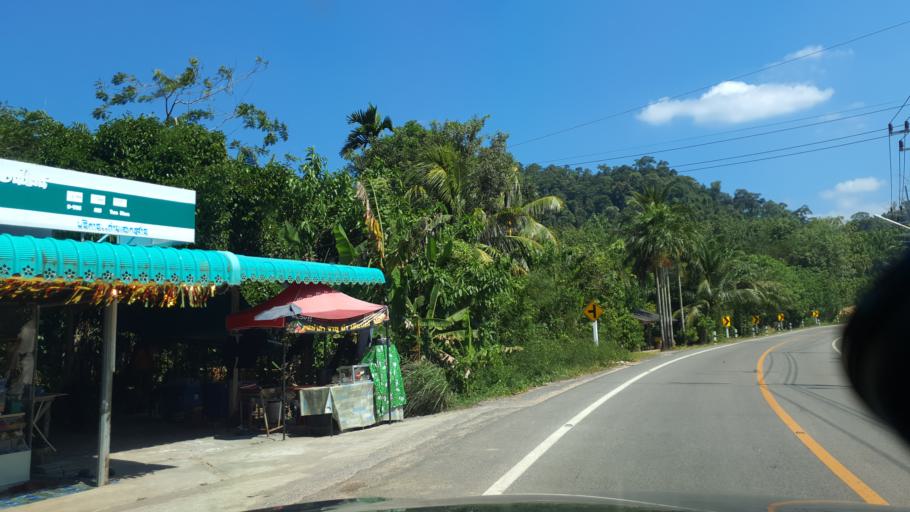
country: TH
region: Krabi
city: Khlong Thom
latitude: 7.9284
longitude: 99.2396
